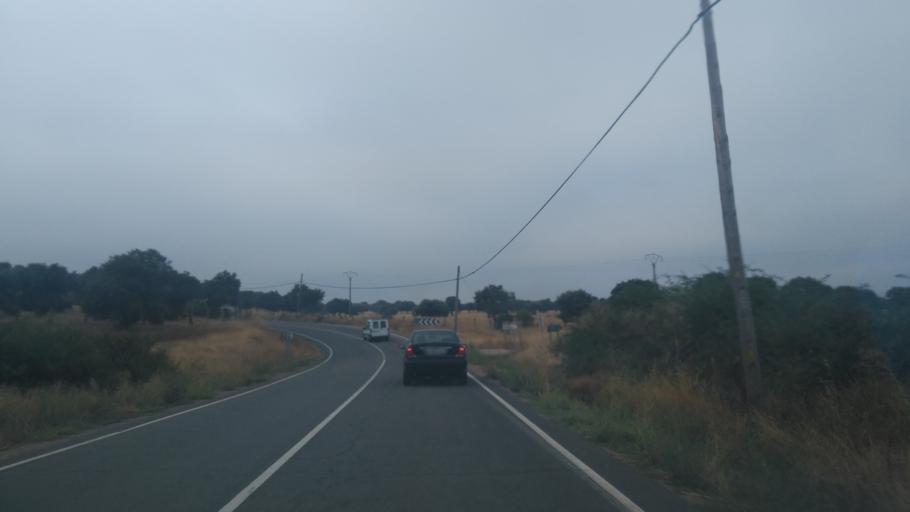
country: ES
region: Castille and Leon
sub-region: Provincia de Salamanca
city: Robliza de Cojos
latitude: 40.8515
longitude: -5.9594
